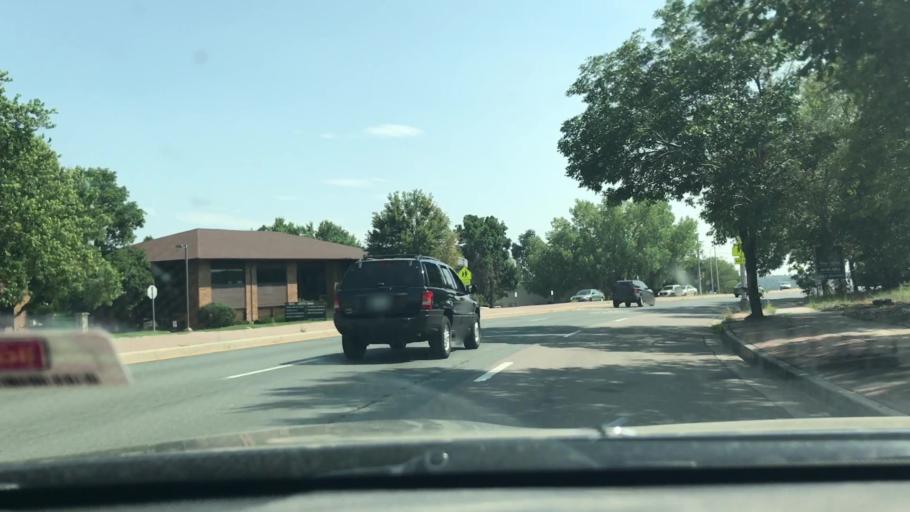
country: US
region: Colorado
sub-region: El Paso County
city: Colorado Springs
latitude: 38.9123
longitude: -104.7751
